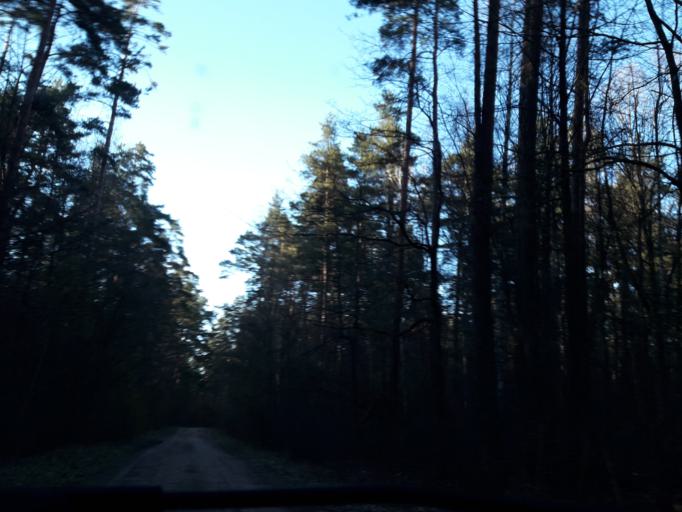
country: LV
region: Kekava
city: Kekava
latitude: 56.8557
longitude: 24.2321
